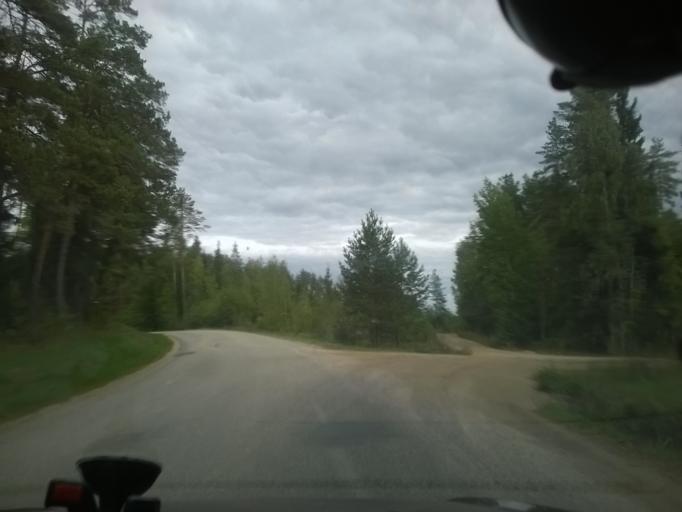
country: EE
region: Vorumaa
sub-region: Voru linn
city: Voru
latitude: 57.8166
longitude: 27.1144
